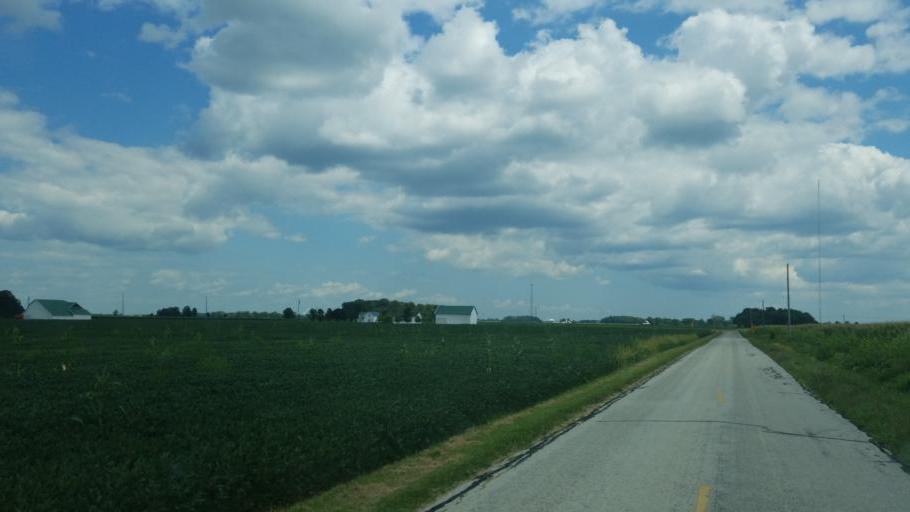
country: US
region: Ohio
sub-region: Ottawa County
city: Elmore
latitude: 41.5016
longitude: -83.2834
